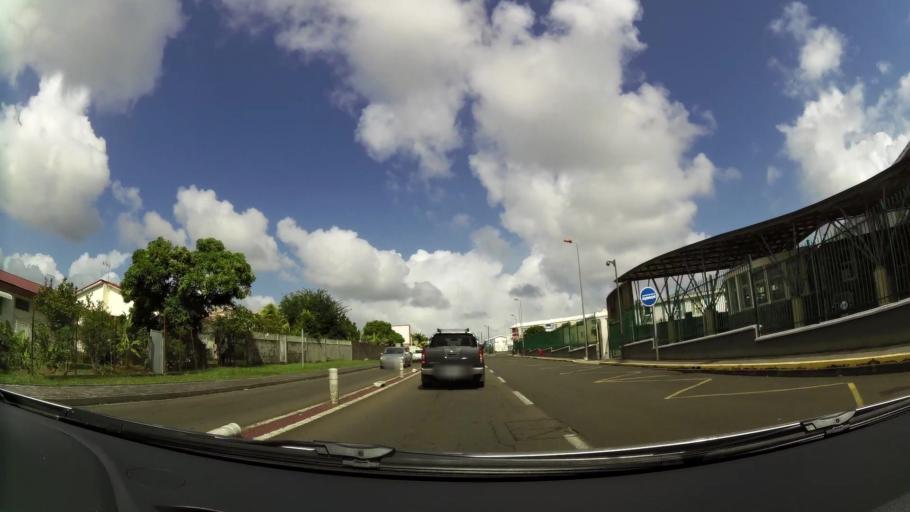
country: MQ
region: Martinique
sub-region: Martinique
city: Le Lamentin
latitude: 14.6168
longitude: -60.9896
